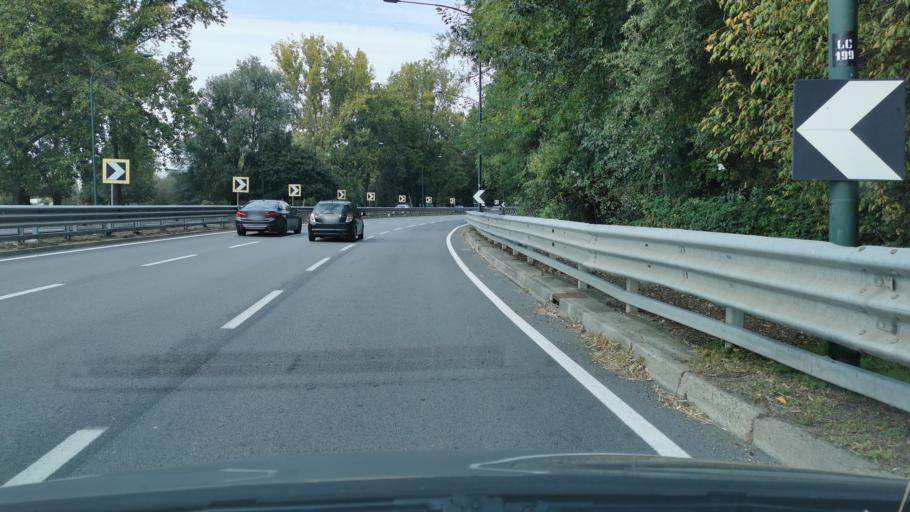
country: IT
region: Piedmont
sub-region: Provincia di Torino
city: San Mauro Torinese
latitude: 45.0880
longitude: 7.7275
